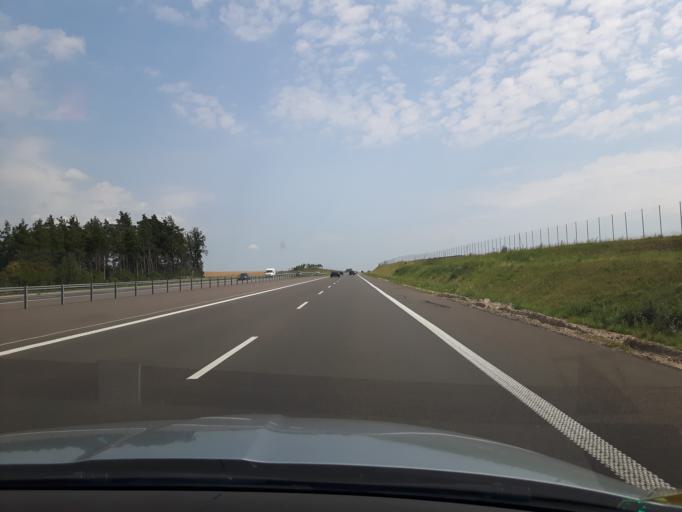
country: PL
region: Warmian-Masurian Voivodeship
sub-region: Powiat nidzicki
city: Nidzica
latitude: 53.3398
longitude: 20.4156
